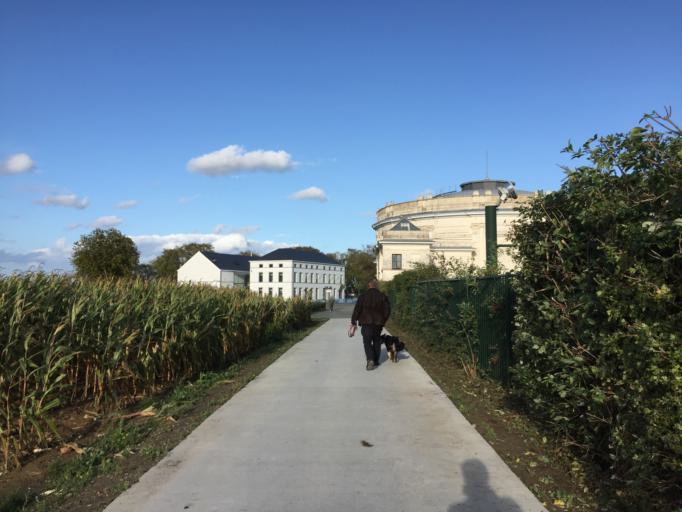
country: BE
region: Wallonia
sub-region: Province du Brabant Wallon
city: Waterloo
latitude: 50.6790
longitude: 4.4039
